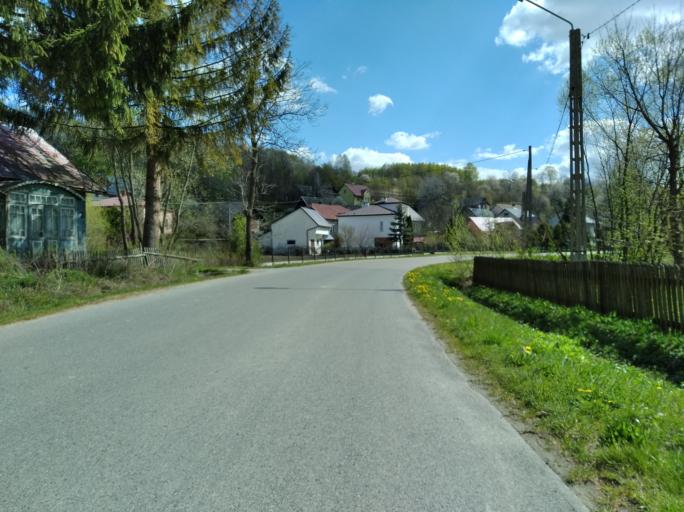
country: PL
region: Subcarpathian Voivodeship
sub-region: Powiat brzozowski
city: Wesola
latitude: 49.8052
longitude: 22.0882
